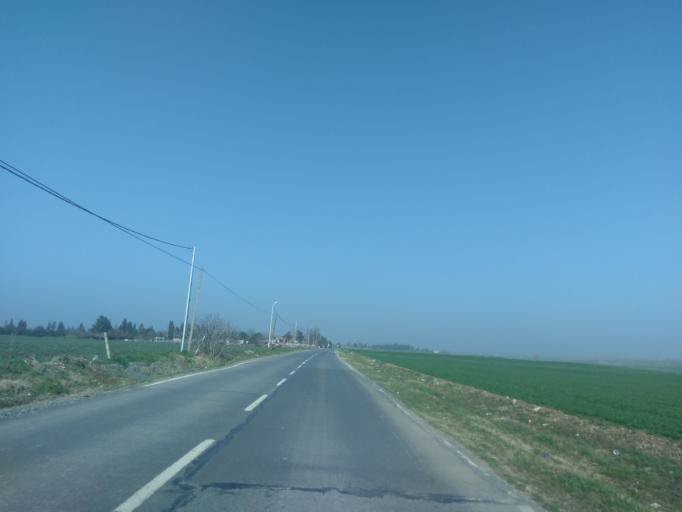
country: TR
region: Istanbul
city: Silivri
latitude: 41.0878
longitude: 28.2687
